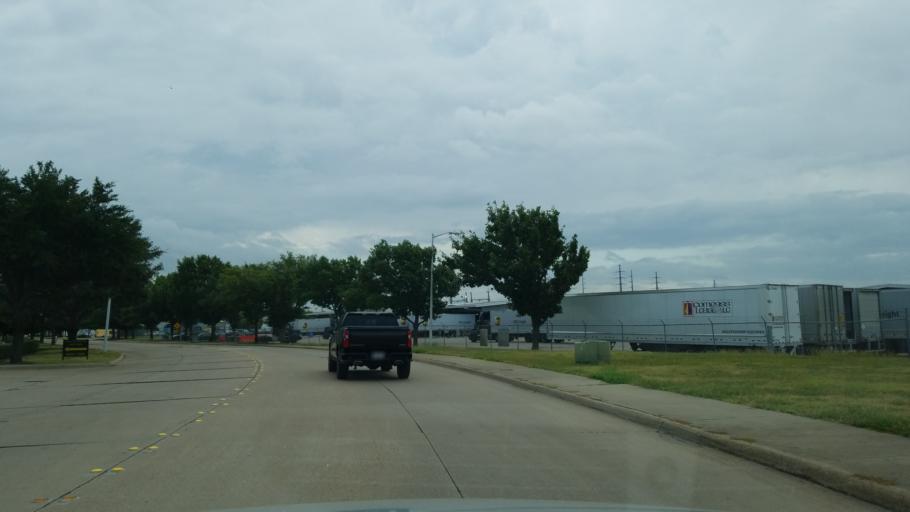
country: US
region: Texas
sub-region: Dallas County
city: Garland
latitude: 32.9039
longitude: -96.6802
